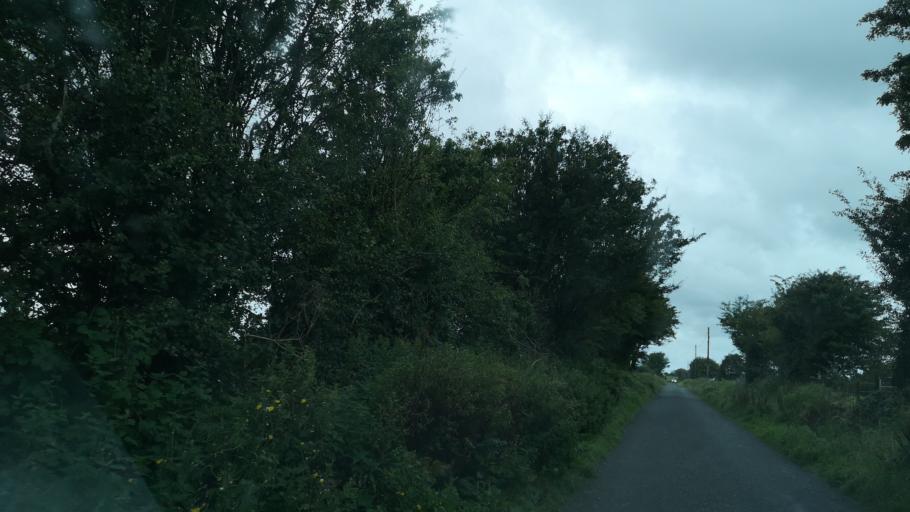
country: IE
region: Connaught
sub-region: County Galway
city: Athenry
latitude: 53.3236
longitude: -8.7573
